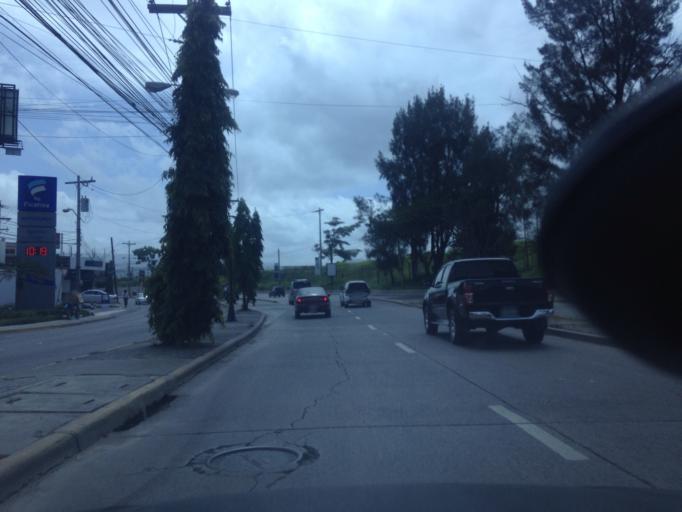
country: HN
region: Francisco Morazan
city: Tegucigalpa
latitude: 14.0652
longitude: -87.2177
